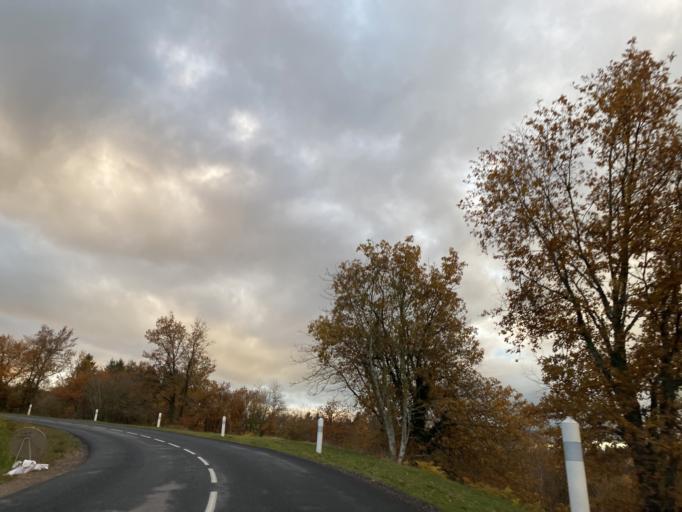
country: FR
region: Auvergne
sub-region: Departement du Puy-de-Dome
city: Cunlhat
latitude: 45.6976
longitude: 3.5830
